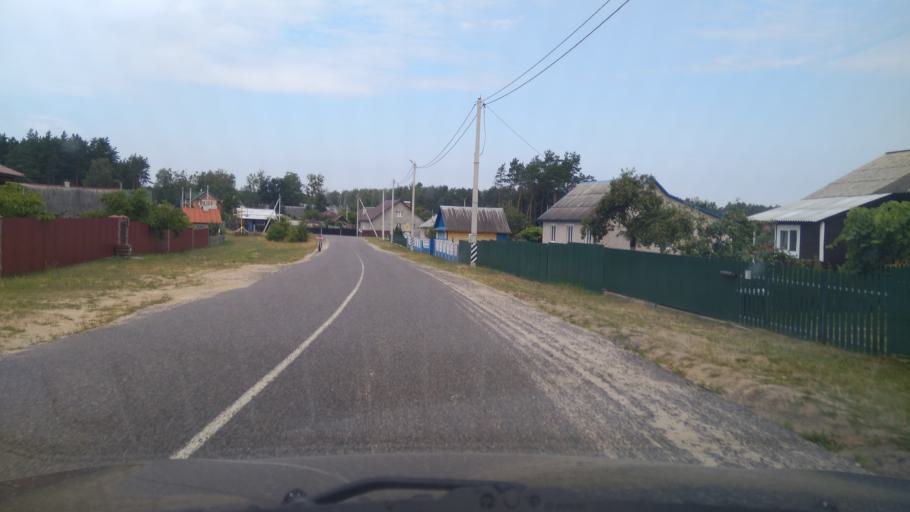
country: BY
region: Brest
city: Nyakhachava
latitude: 52.6097
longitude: 25.0884
